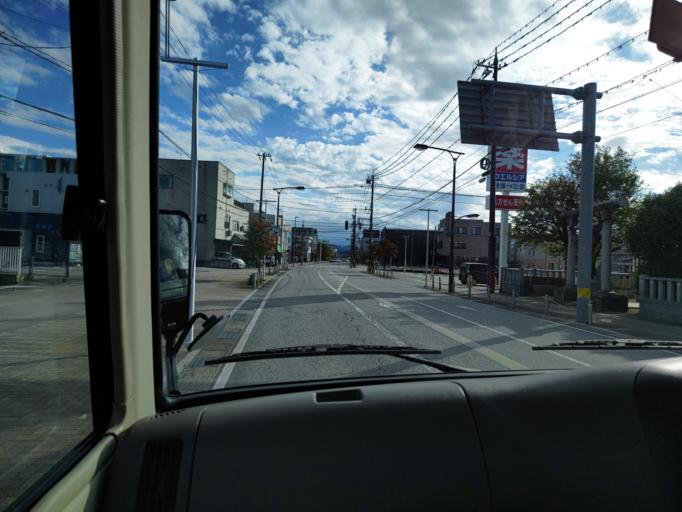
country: JP
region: Toyama
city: Nyuzen
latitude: 36.8726
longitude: 137.4471
